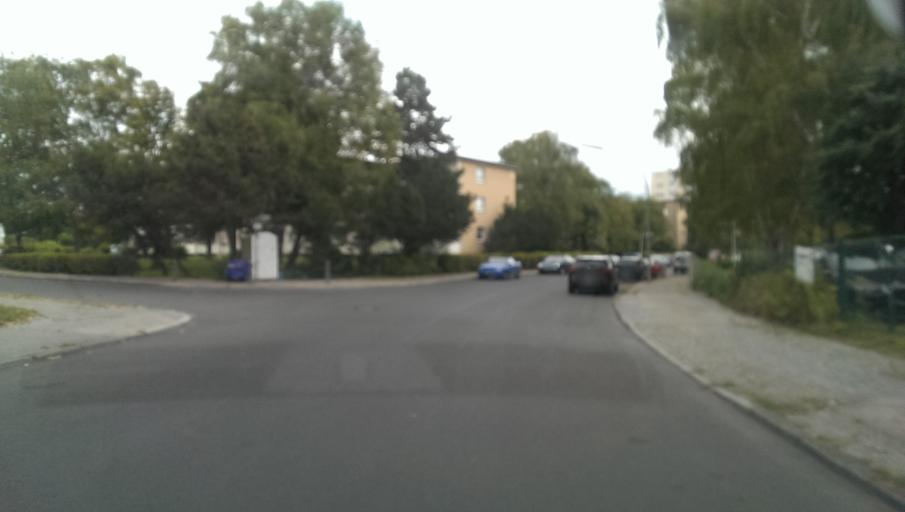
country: DE
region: Berlin
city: Britz
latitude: 52.4240
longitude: 13.4286
